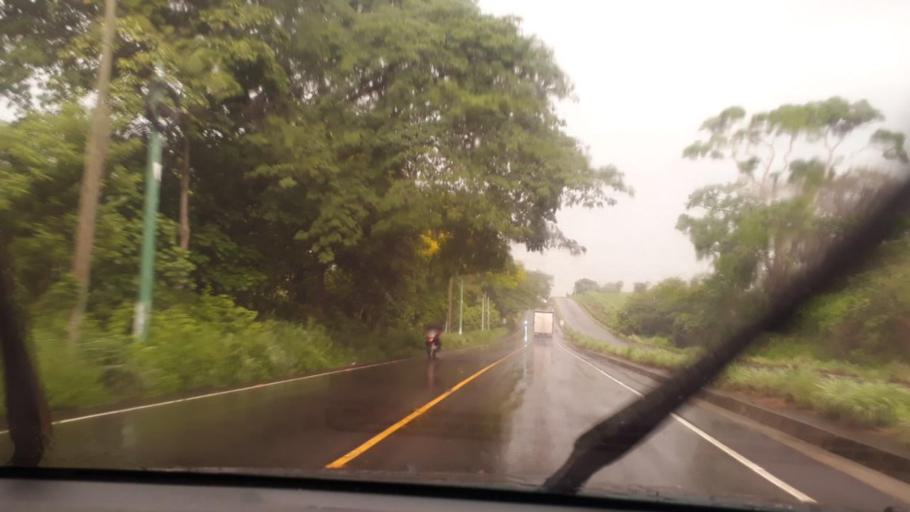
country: GT
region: Santa Rosa
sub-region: Municipio de Taxisco
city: Taxisco
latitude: 14.0908
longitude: -90.5121
